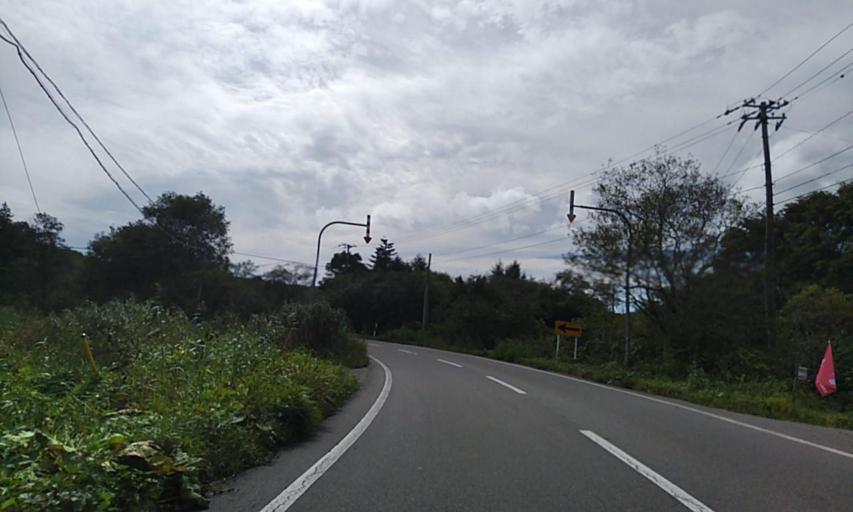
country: JP
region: Hokkaido
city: Kushiro
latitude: 42.8445
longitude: 143.8426
